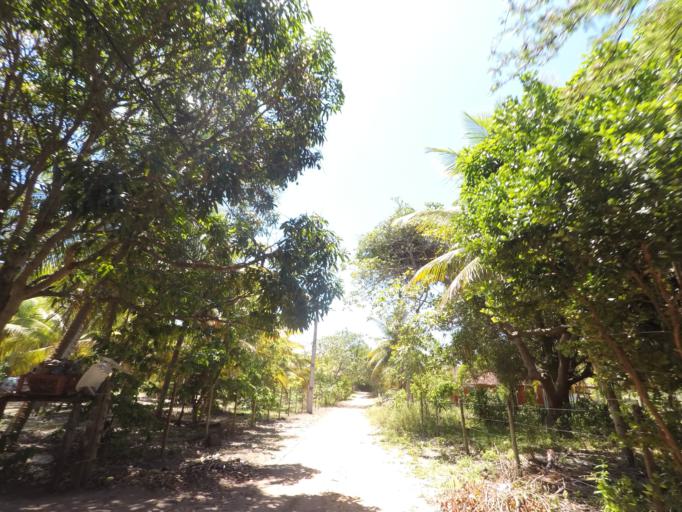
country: BR
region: Bahia
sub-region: Marau
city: Marau
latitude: -14.0210
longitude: -38.9474
